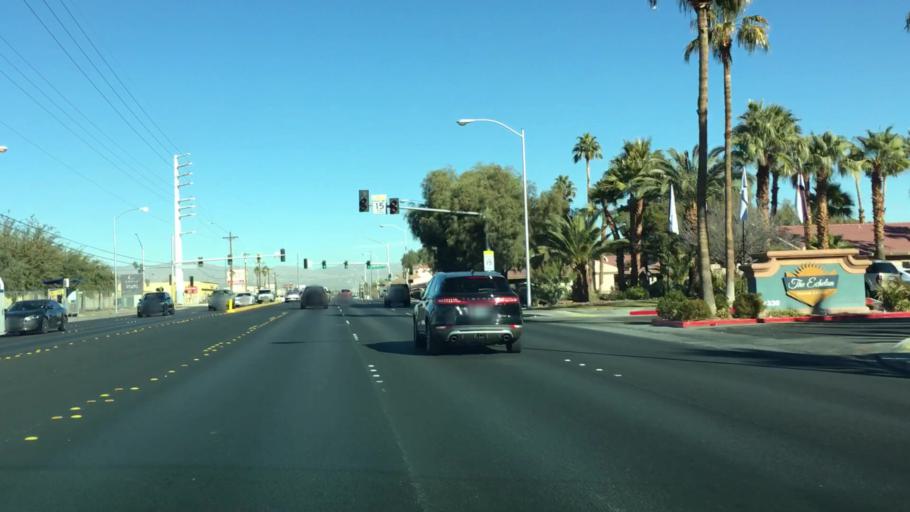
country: US
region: Nevada
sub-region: Clark County
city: Winchester
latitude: 36.1098
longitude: -115.1191
